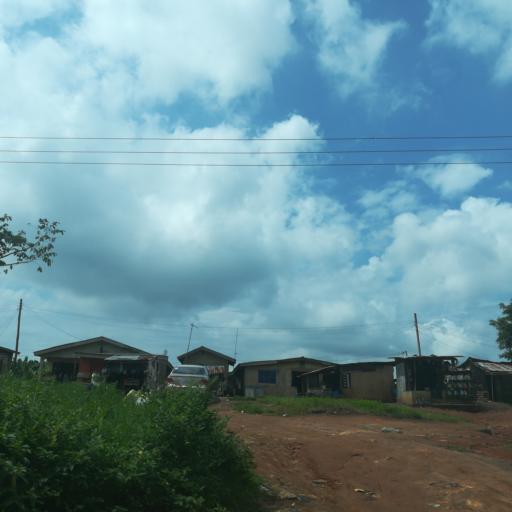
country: NG
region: Lagos
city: Ejirin
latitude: 6.6495
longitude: 3.7108
